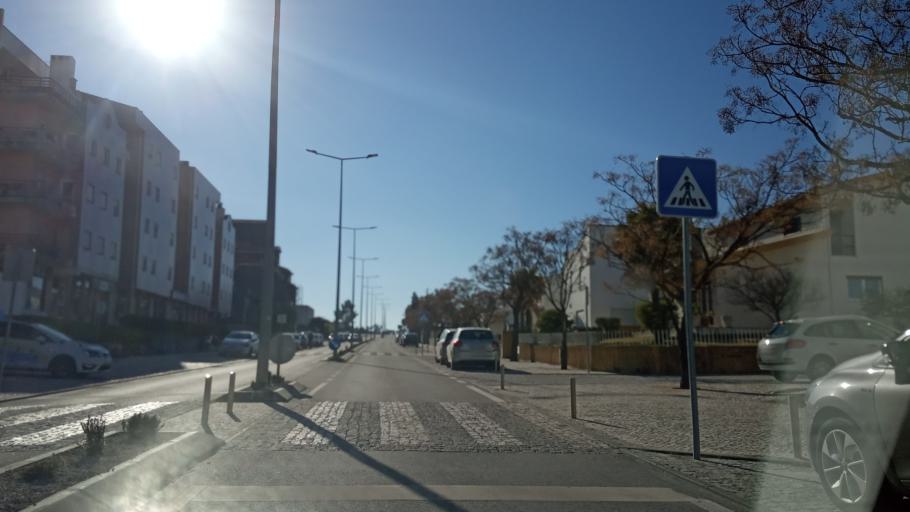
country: PT
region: Aveiro
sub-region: Anadia
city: Anadia
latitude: 40.4377
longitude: -8.4385
